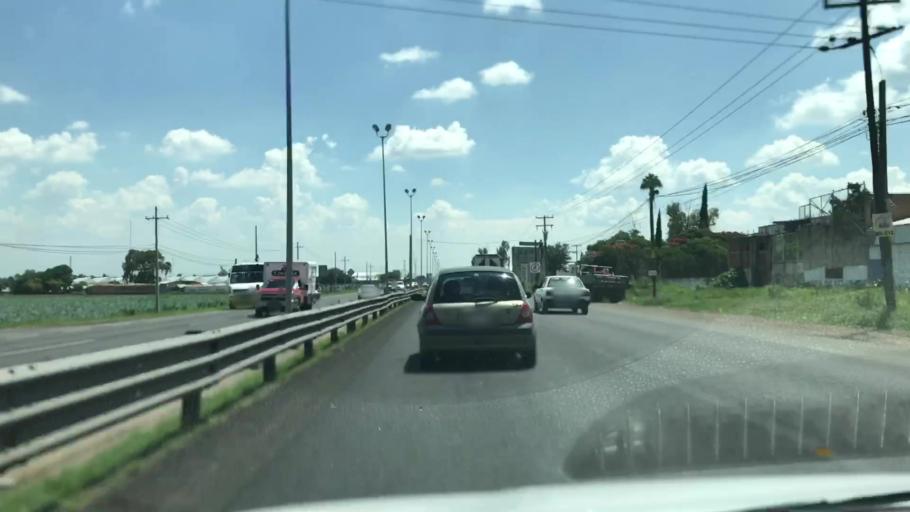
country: MX
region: Guanajuato
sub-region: Irapuato
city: Fraccionamiento las Liebres
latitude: 20.6410
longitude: -101.3810
